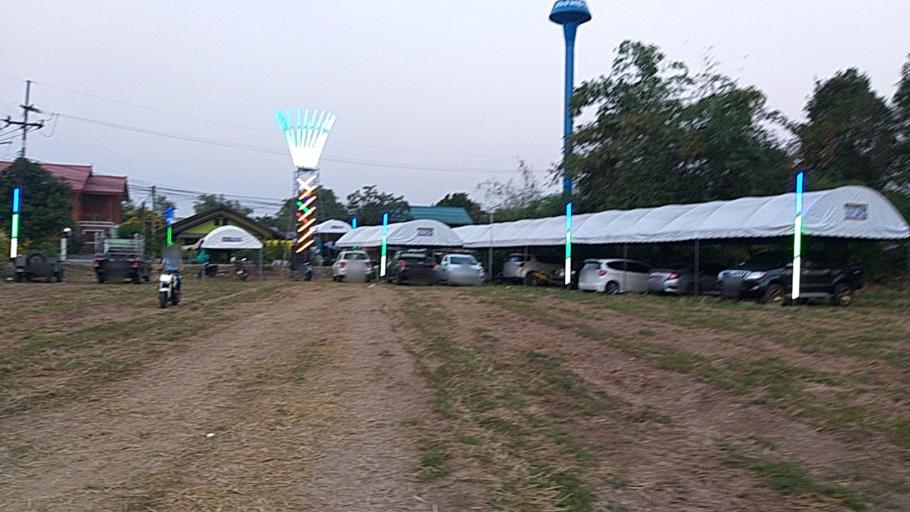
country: TH
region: Sing Buri
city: Sing Buri
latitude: 14.8354
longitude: 100.4014
